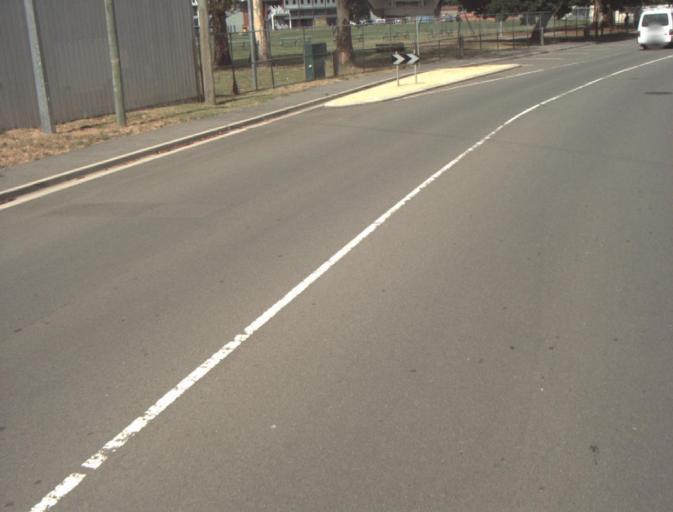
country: AU
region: Tasmania
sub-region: Launceston
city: Launceston
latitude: -41.4227
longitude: 147.1396
